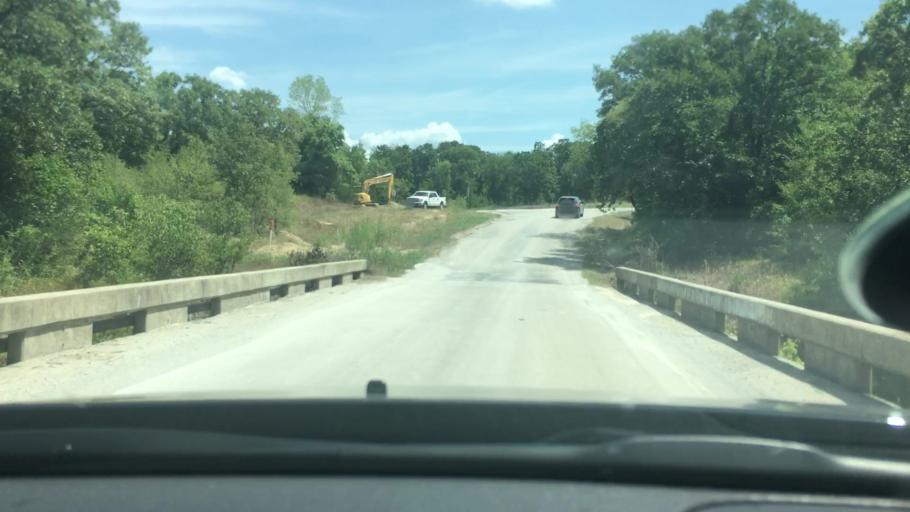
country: US
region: Oklahoma
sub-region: Carter County
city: Ardmore
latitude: 34.0744
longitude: -97.1788
